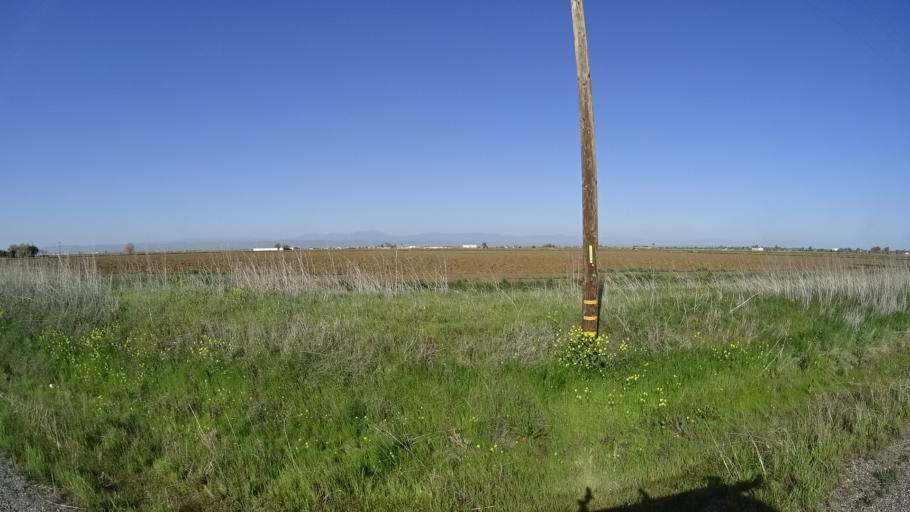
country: US
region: California
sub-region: Glenn County
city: Willows
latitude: 39.4971
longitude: -122.1744
